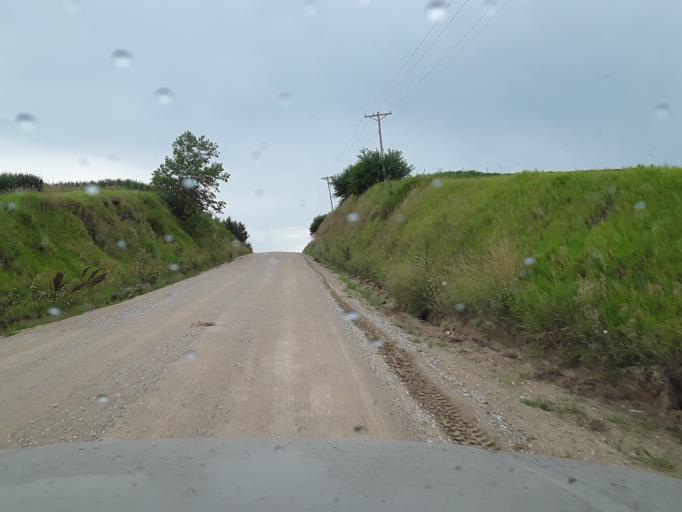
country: US
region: Nebraska
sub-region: Washington County
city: Blair
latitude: 41.5092
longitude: -96.1775
